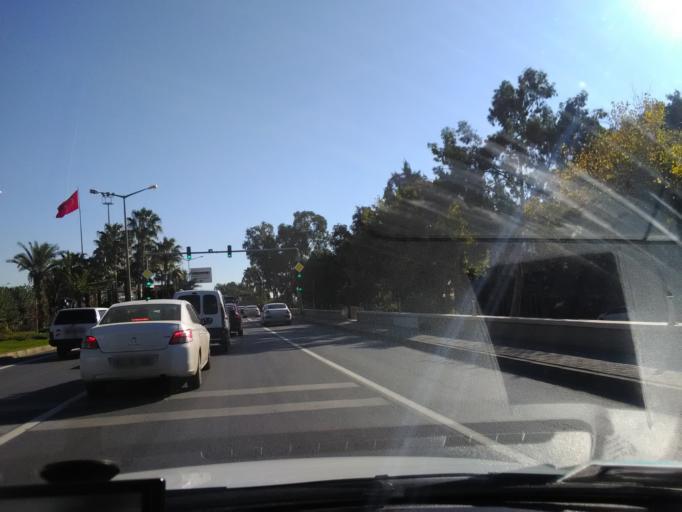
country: TR
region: Antalya
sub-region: Alanya
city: Mahmutlar
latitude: 36.5179
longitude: 32.0609
